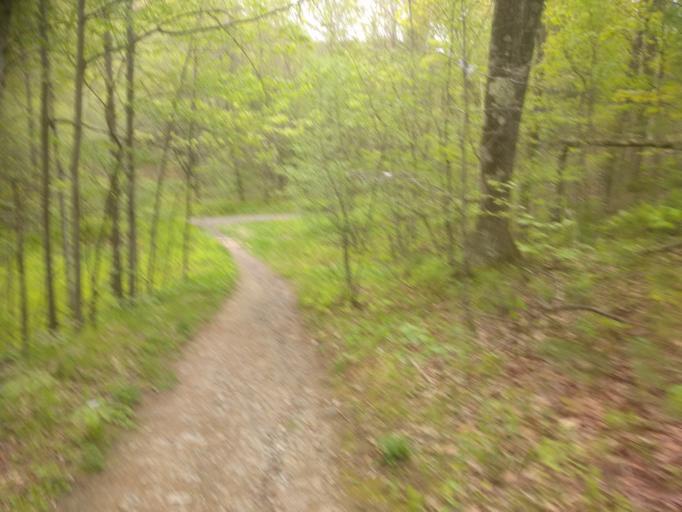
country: CA
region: Quebec
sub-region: Outaouais
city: Wakefield
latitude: 45.5330
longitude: -75.9942
